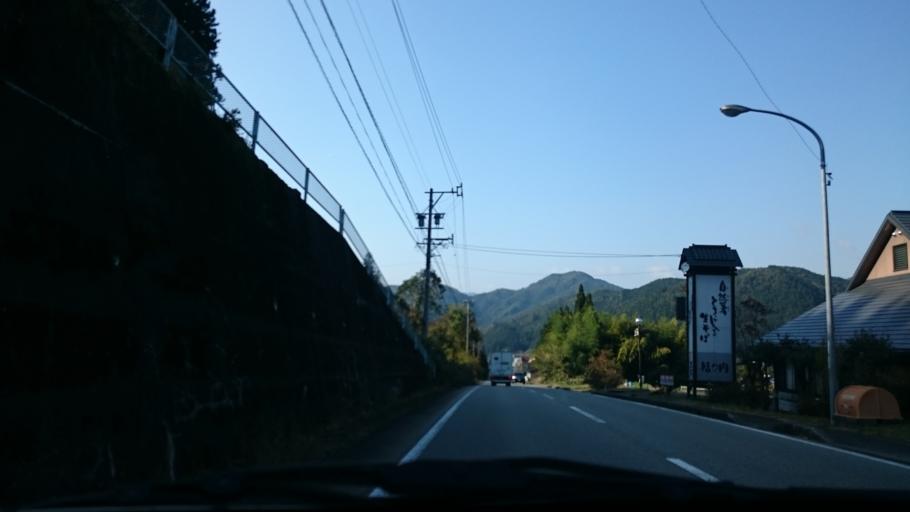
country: JP
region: Gifu
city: Gujo
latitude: 35.7624
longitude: 137.2928
